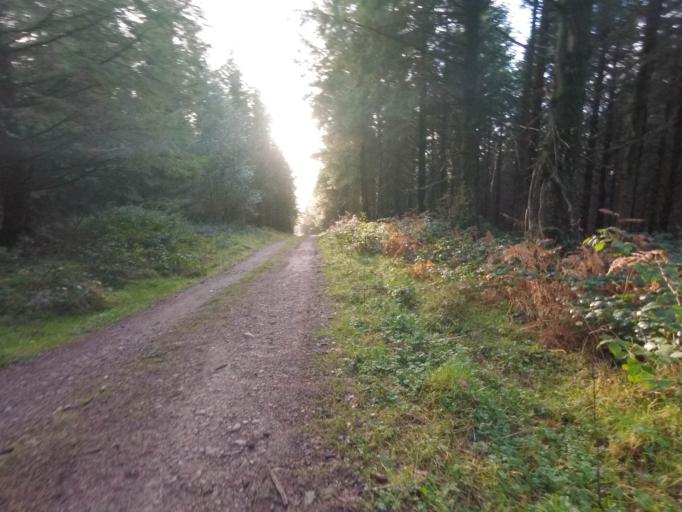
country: IE
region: Munster
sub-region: Waterford
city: Portlaw
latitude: 52.3150
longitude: -7.3471
